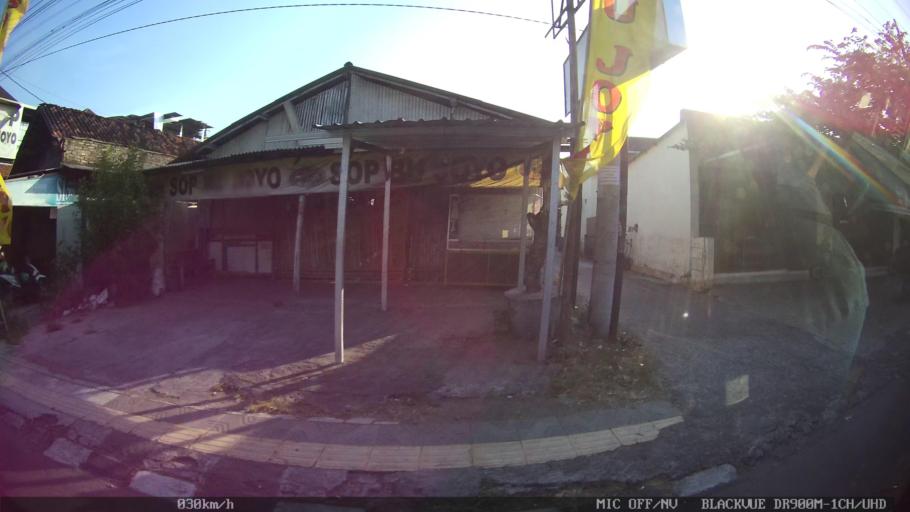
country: ID
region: Daerah Istimewa Yogyakarta
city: Yogyakarta
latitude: -7.8200
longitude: 110.3882
